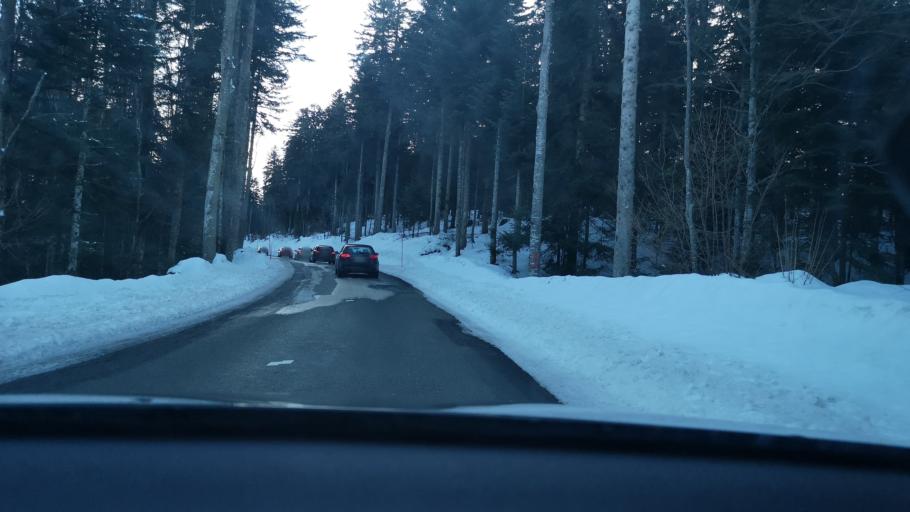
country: FR
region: Franche-Comte
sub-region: Departement du Doubs
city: Gilley
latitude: 46.9746
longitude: 6.4882
